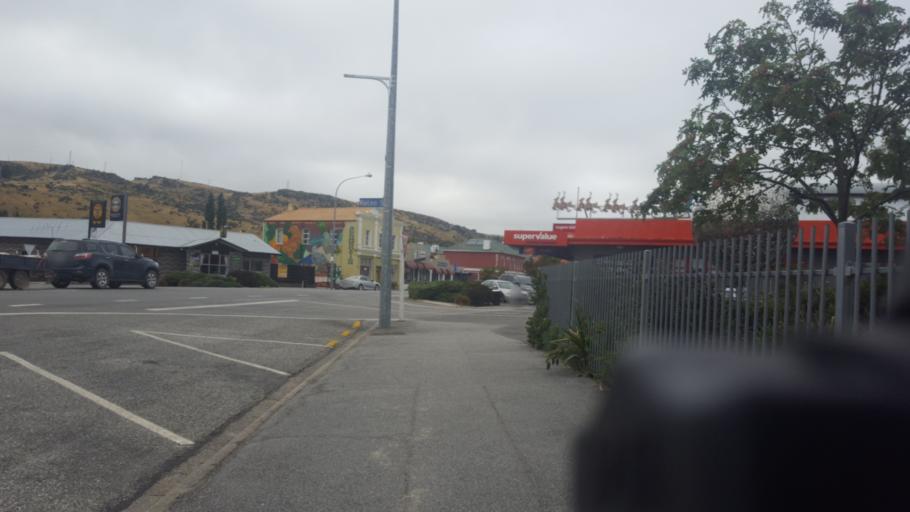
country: NZ
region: Otago
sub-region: Queenstown-Lakes District
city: Kingston
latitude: -45.5398
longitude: 169.3136
